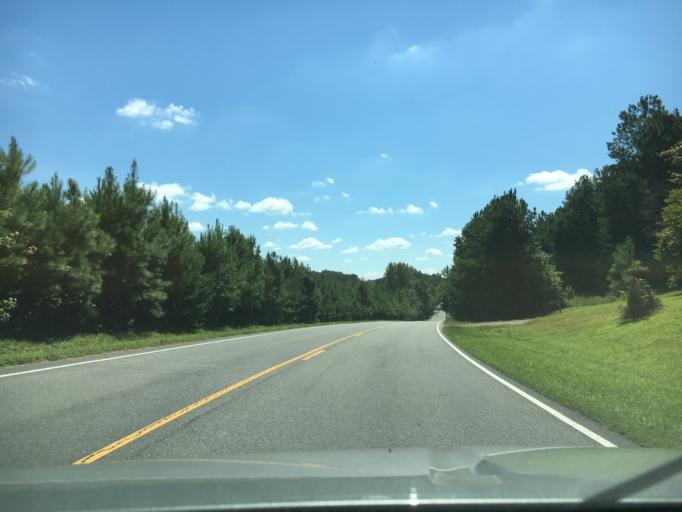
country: US
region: Virginia
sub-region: Amelia County
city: Amelia Court House
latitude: 37.4077
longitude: -77.8933
